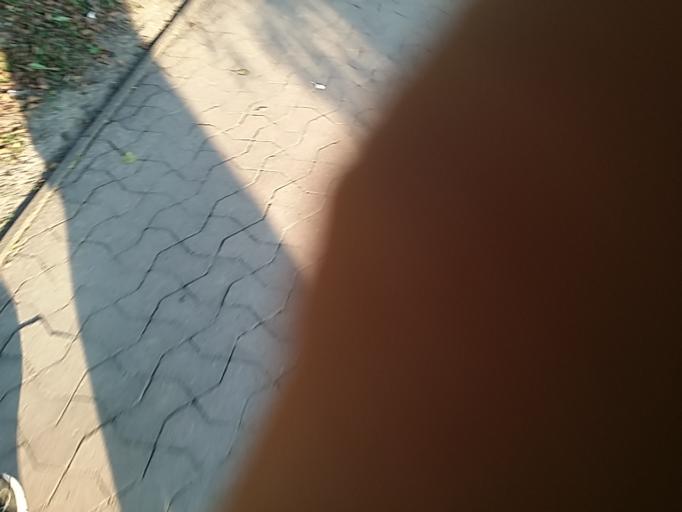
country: HU
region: Baranya
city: Pellerd
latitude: 46.1388
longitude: 18.1144
